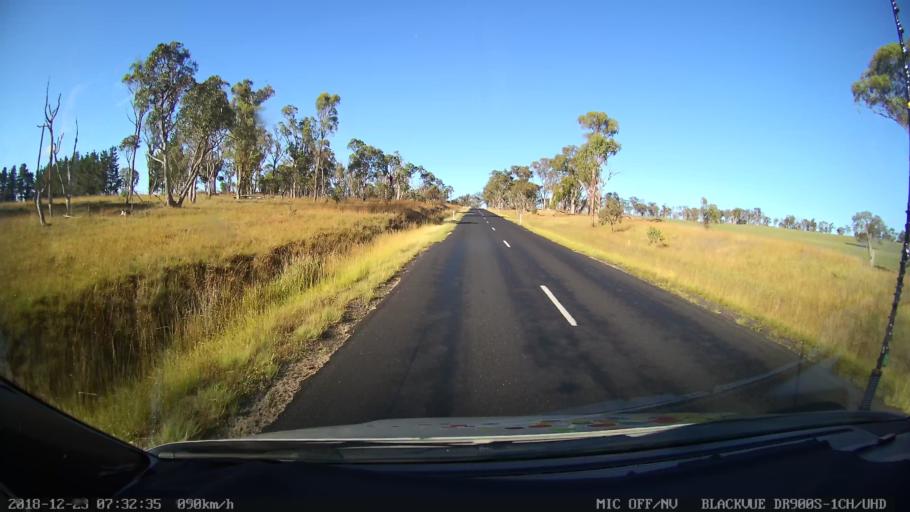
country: AU
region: New South Wales
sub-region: Armidale Dumaresq
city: Enmore
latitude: -30.5057
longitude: 152.1148
